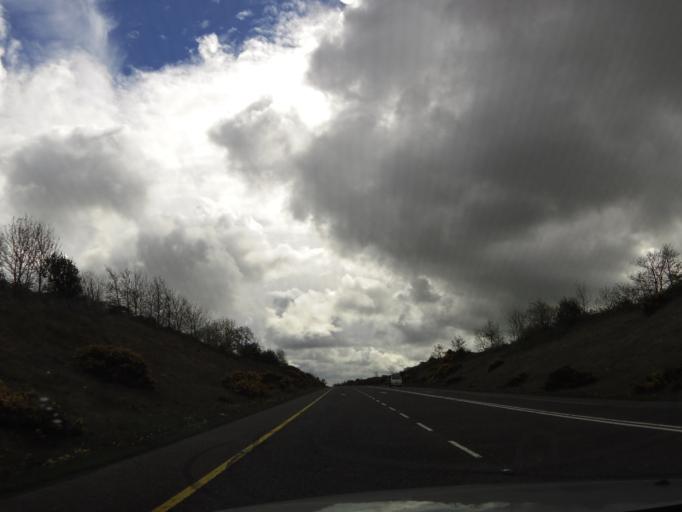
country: IE
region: Connaught
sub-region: Maigh Eo
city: Claremorris
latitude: 53.7647
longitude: -8.9600
